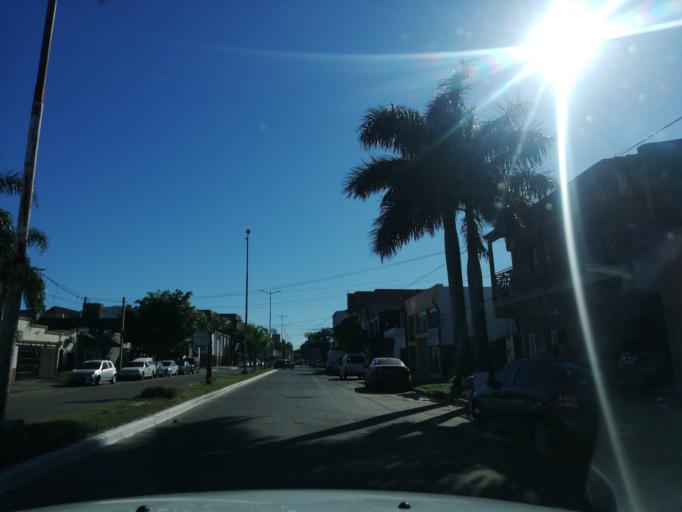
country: AR
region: Corrientes
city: Corrientes
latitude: -27.4730
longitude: -58.8132
